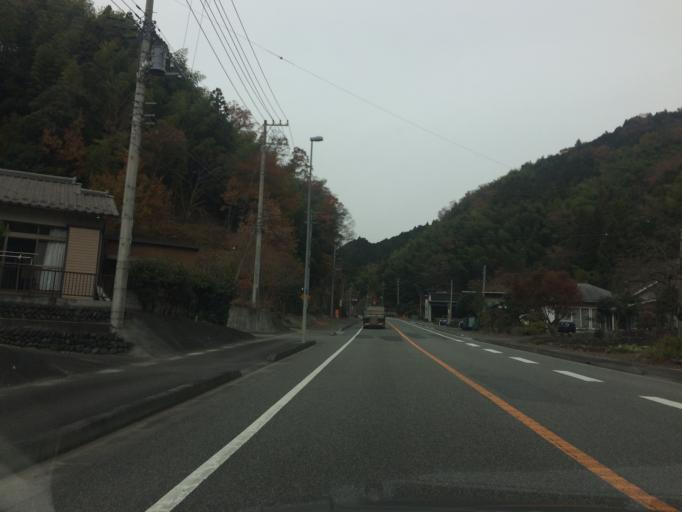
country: JP
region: Shizuoka
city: Fujinomiya
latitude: 35.2651
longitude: 138.4619
